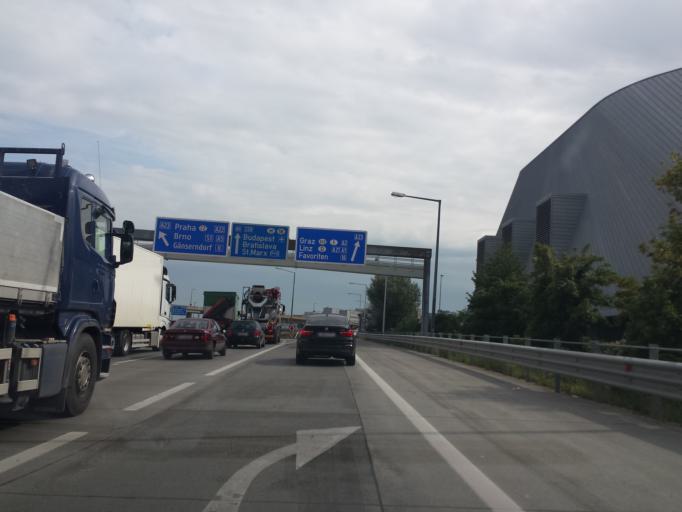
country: AT
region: Vienna
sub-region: Wien Stadt
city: Vienna
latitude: 48.1819
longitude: 16.3994
